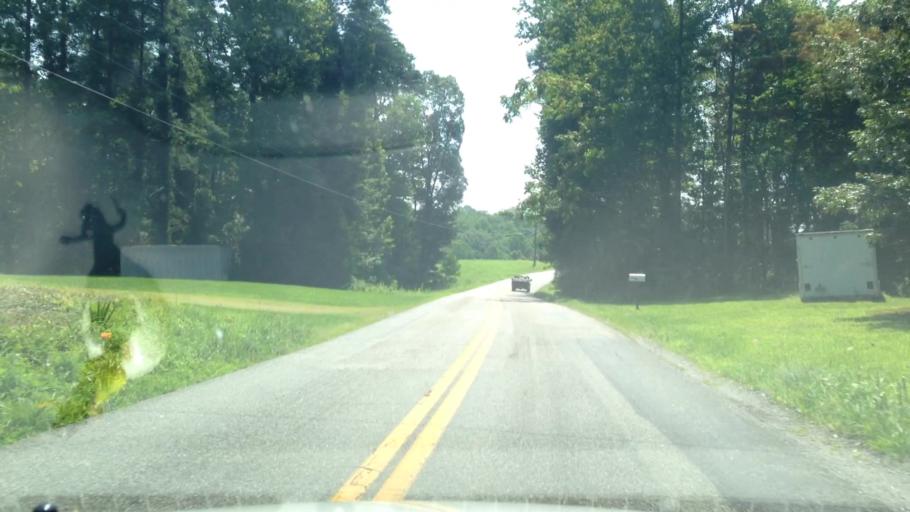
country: US
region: Virginia
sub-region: Patrick County
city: Stuart
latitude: 36.5779
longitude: -80.2456
